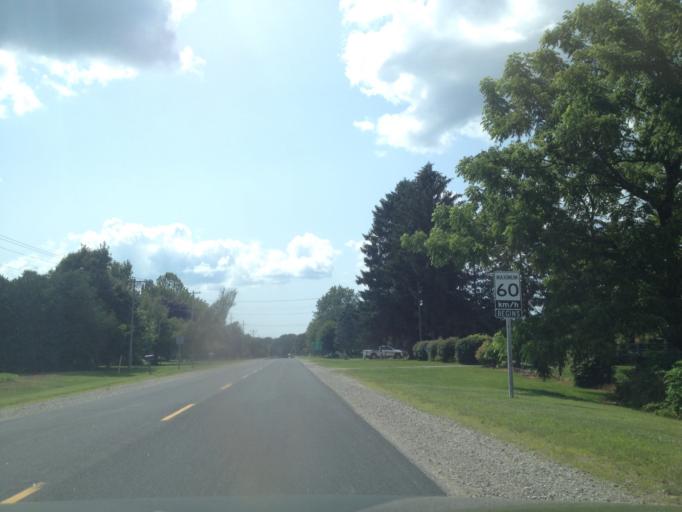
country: CA
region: Ontario
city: Aylmer
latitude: 42.6759
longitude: -80.9795
